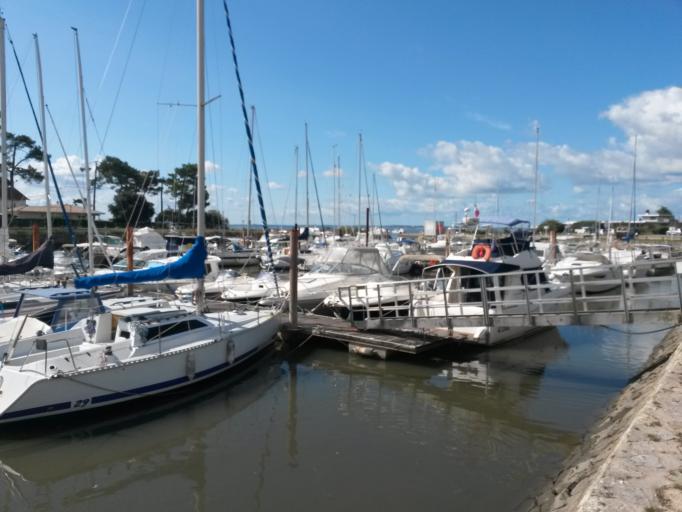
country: FR
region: Aquitaine
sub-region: Departement de la Gironde
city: Andernos-les-Bains
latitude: 44.7232
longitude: -1.0759
